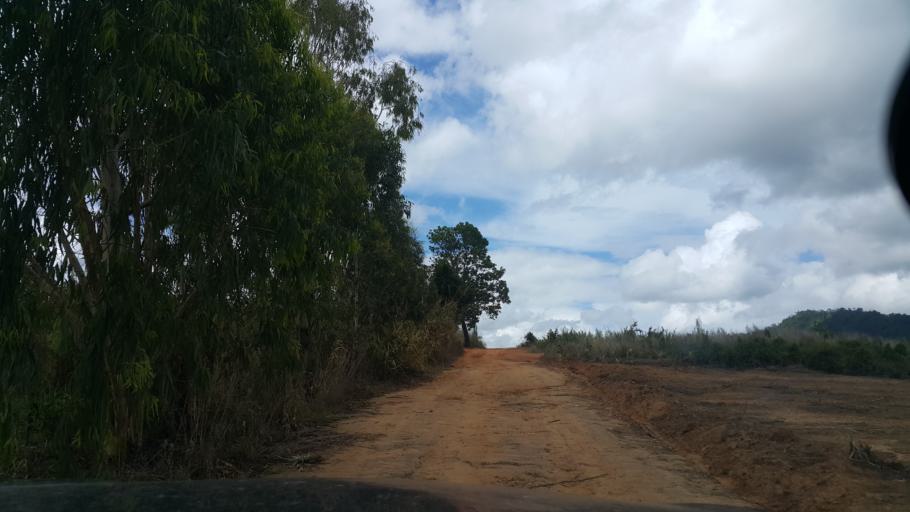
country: TH
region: Loei
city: Na Haeo
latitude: 17.5919
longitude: 100.8961
